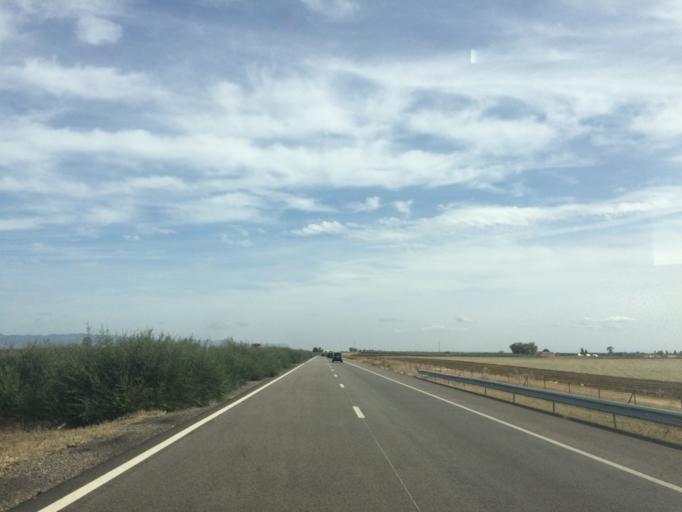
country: MA
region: Meknes-Tafilalet
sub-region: Meknes
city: Meknes
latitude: 33.8925
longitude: -5.7003
